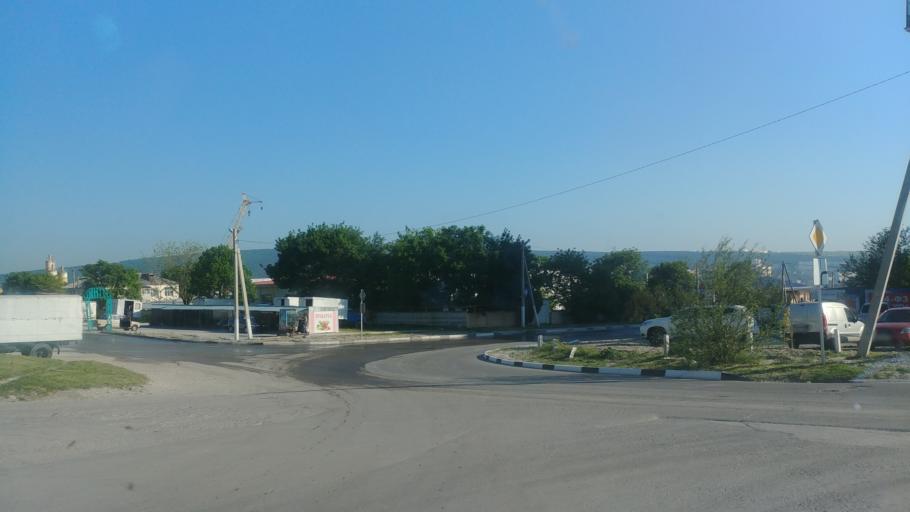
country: RU
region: Krasnodarskiy
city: Gelendzhik
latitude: 44.5719
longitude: 38.0928
